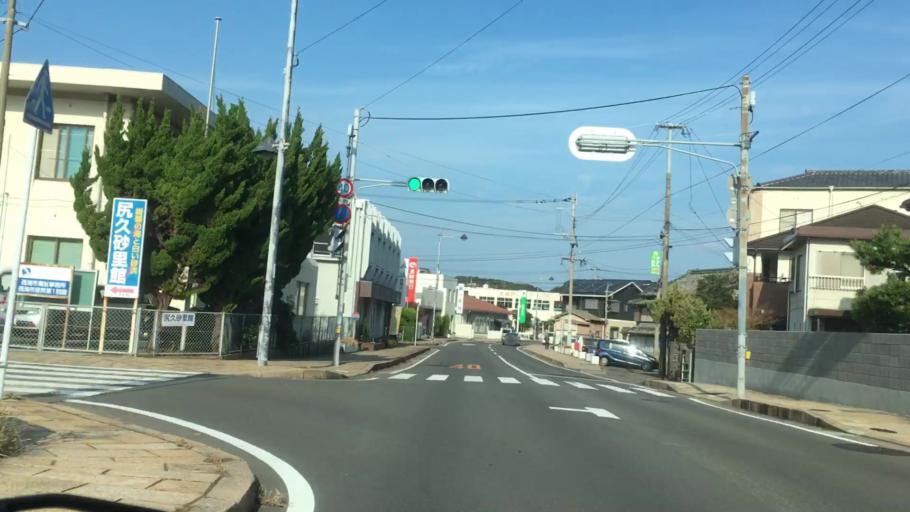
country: JP
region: Nagasaki
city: Togitsu
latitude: 32.9328
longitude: 129.6422
